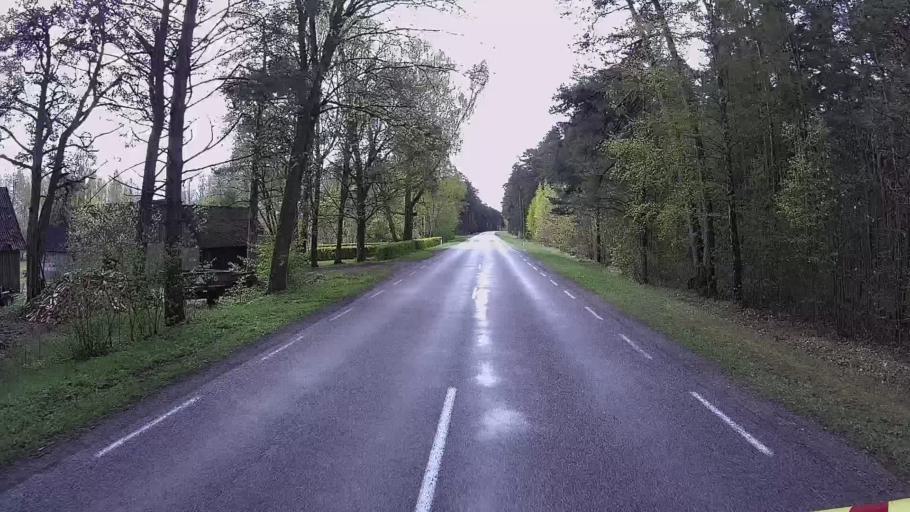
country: EE
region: Hiiumaa
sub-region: Kaerdla linn
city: Kardla
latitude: 58.7196
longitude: 22.6164
